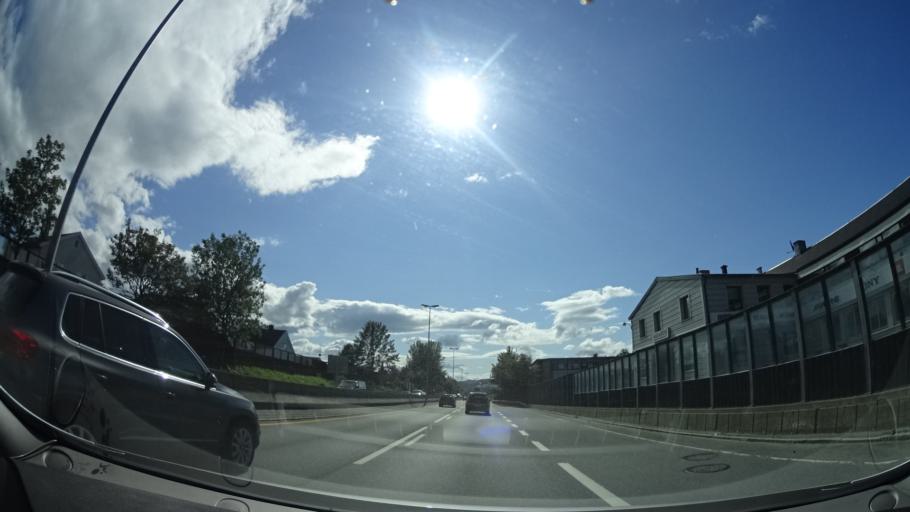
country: NO
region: Sor-Trondelag
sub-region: Trondheim
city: Trondheim
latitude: 63.4068
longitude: 10.4190
